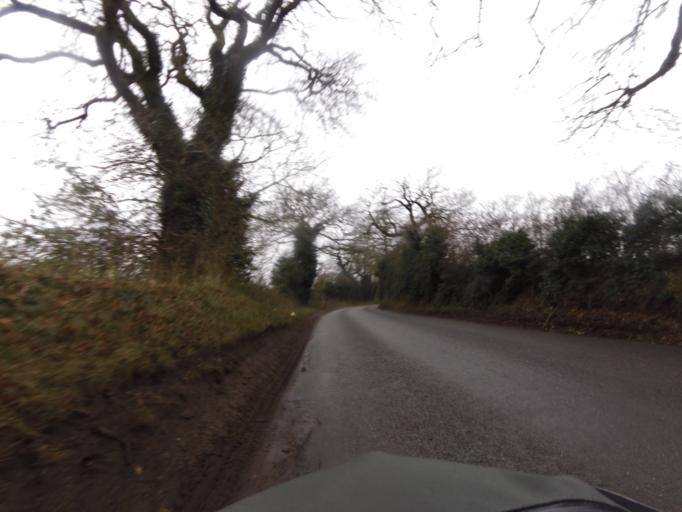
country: GB
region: England
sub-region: Norfolk
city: Briston
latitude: 52.8697
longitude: 1.0745
